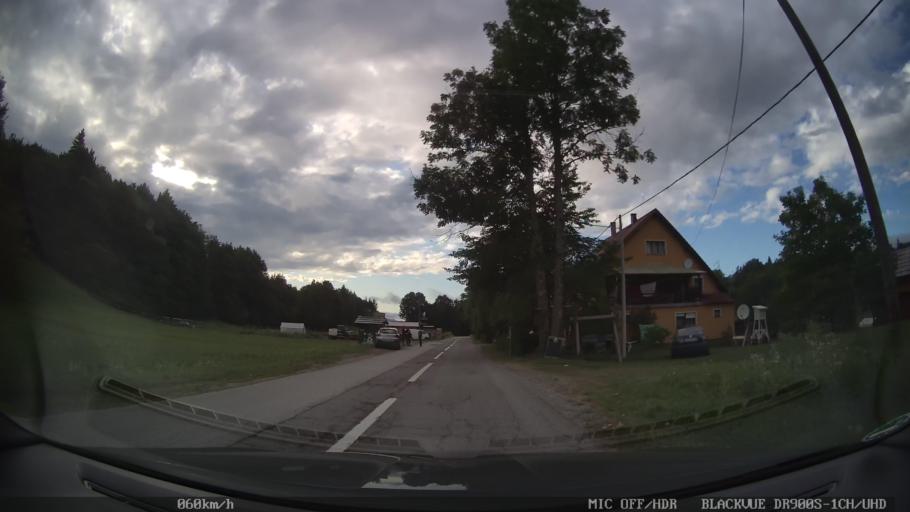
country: HR
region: Licko-Senjska
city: Jezerce
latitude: 44.9653
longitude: 15.5214
